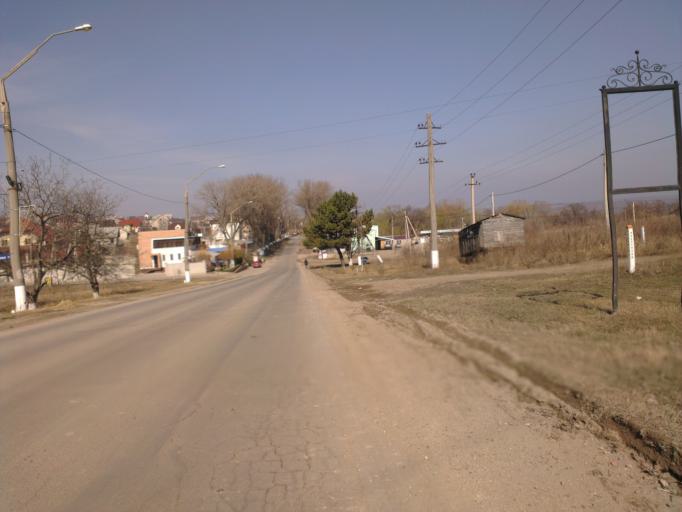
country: MD
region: Chisinau
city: Cricova
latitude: 47.1240
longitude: 28.8658
